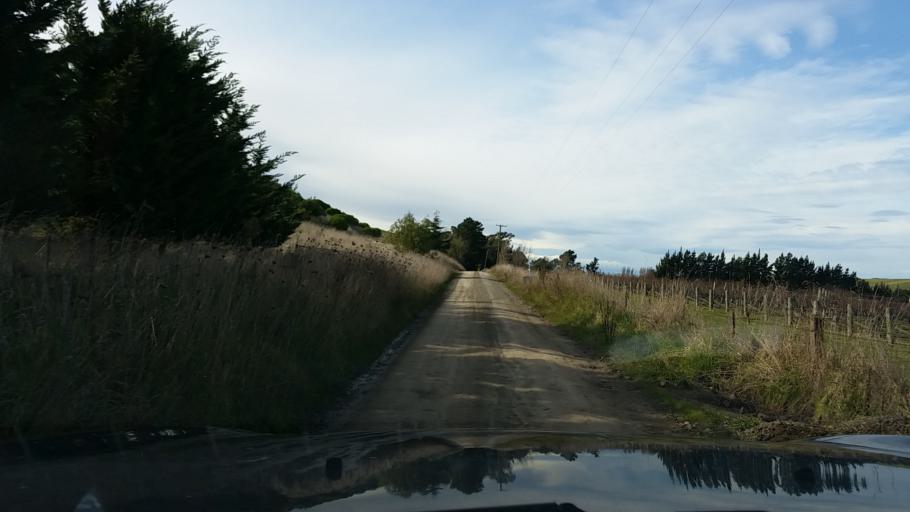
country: NZ
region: Marlborough
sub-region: Marlborough District
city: Blenheim
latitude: -41.5984
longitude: 174.1341
